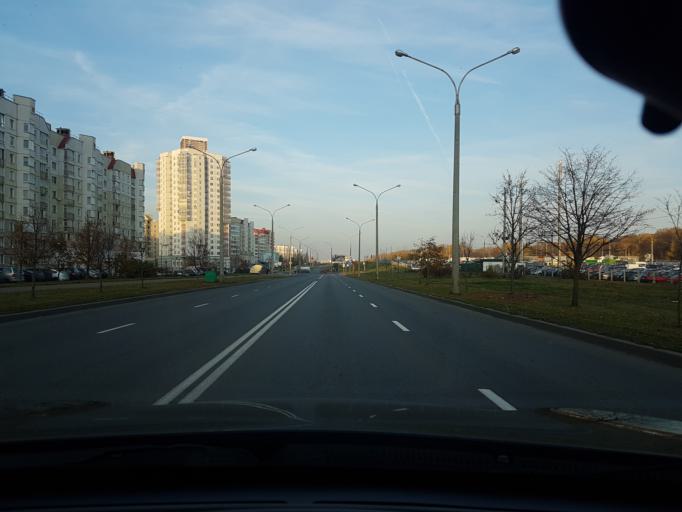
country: BY
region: Minsk
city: Shchomyslitsa
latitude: 53.8450
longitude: 27.4852
